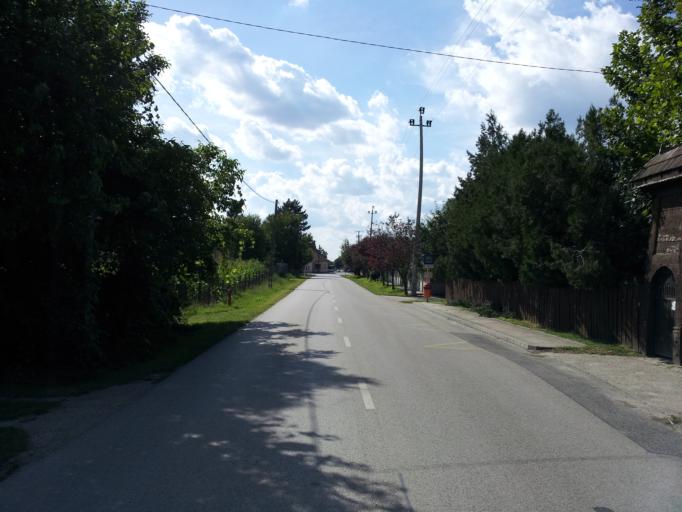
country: HU
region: Pest
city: Szigetcsep
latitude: 47.2626
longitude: 19.0002
